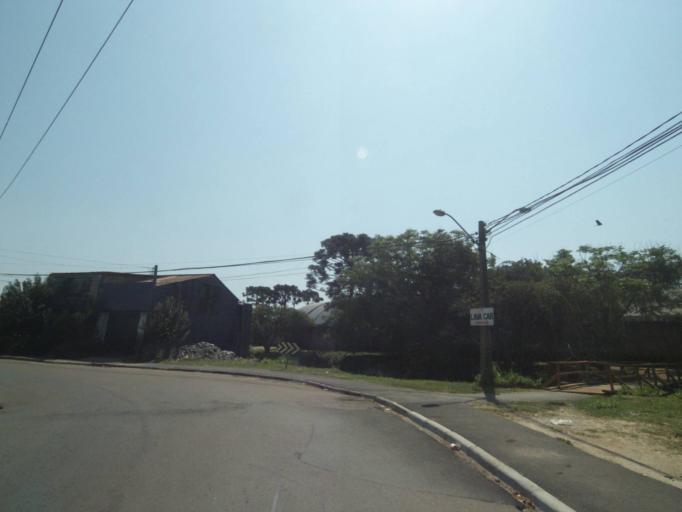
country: BR
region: Parana
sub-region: Sao Jose Dos Pinhais
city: Sao Jose dos Pinhais
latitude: -25.5169
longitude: -49.2706
